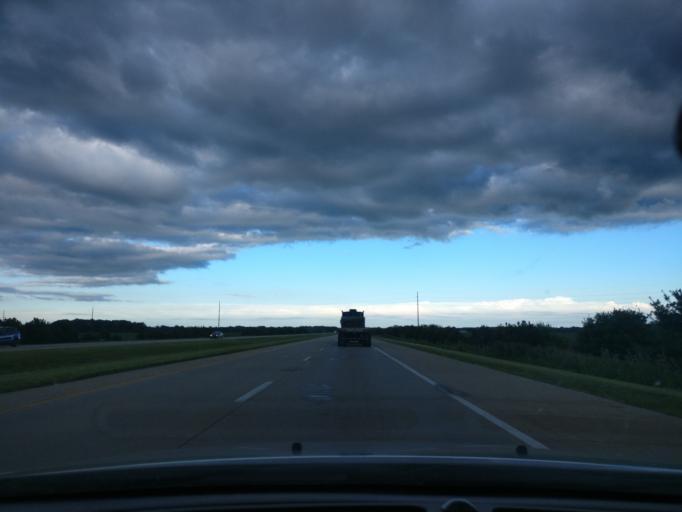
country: US
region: Ohio
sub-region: Greene County
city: Wilberforce
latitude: 39.6829
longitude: -83.8375
